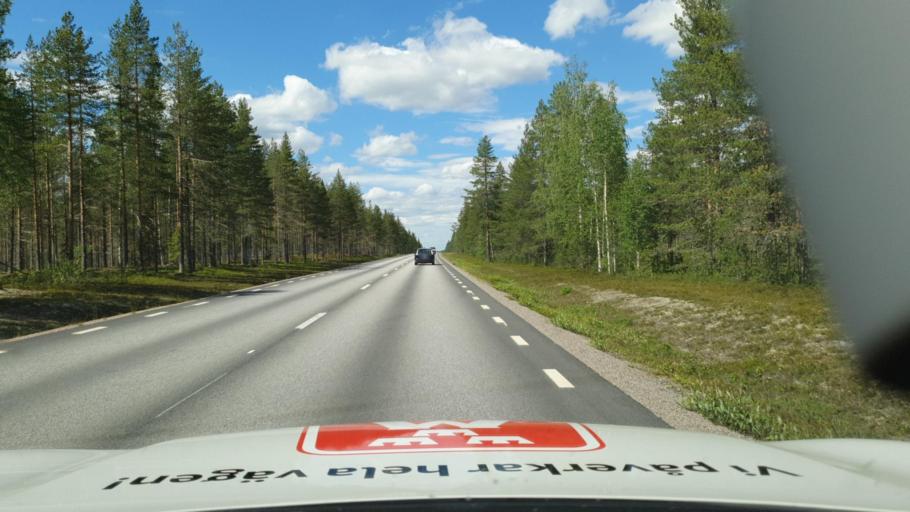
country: SE
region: Vaesterbotten
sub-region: Skelleftea Kommun
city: Langsele
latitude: 65.0098
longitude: 20.1684
